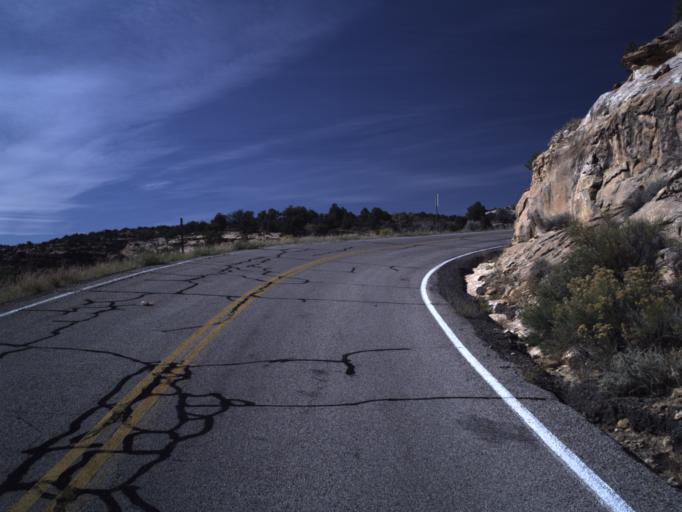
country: US
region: Utah
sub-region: San Juan County
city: Monticello
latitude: 37.9831
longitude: -109.5029
